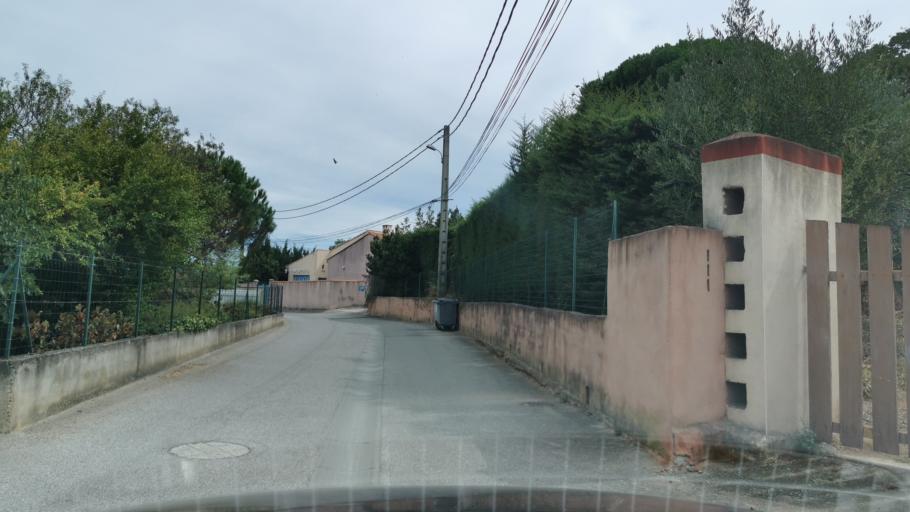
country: FR
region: Languedoc-Roussillon
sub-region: Departement de l'Aude
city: Marcorignan
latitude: 43.2259
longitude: 2.9270
